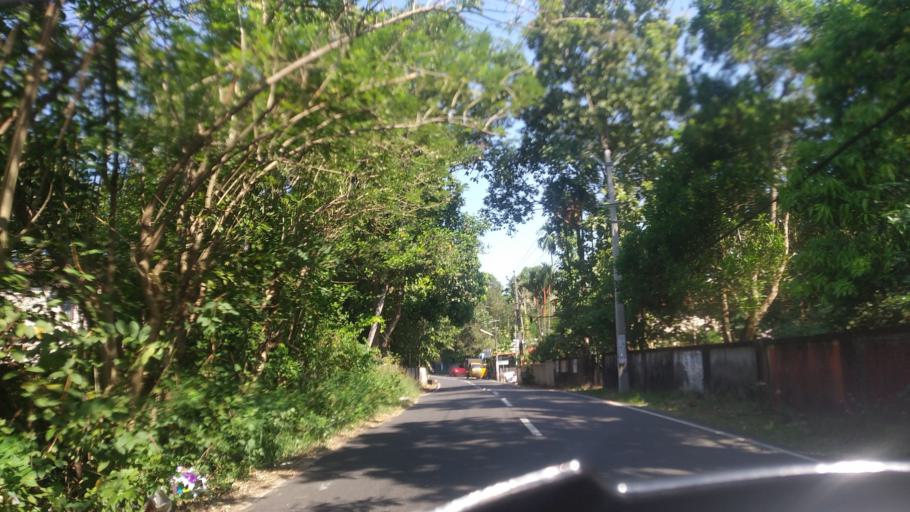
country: IN
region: Kerala
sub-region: Ernakulam
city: Elur
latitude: 10.1107
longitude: 76.2487
